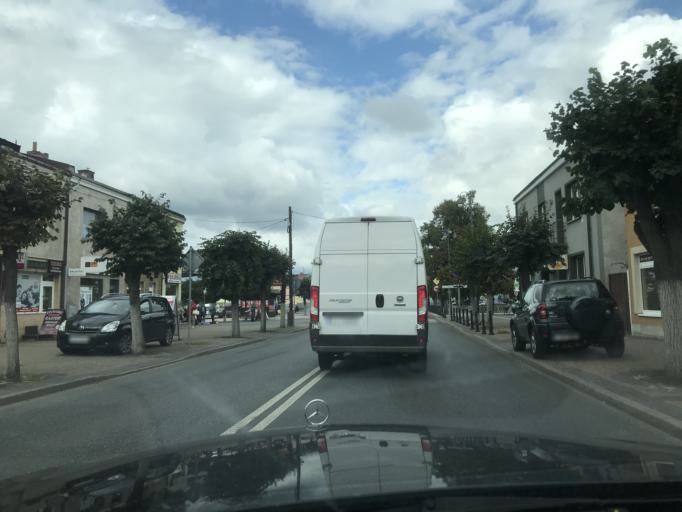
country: PL
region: Lublin Voivodeship
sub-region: Powiat janowski
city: Janow Lubelski
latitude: 50.7061
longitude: 22.4119
